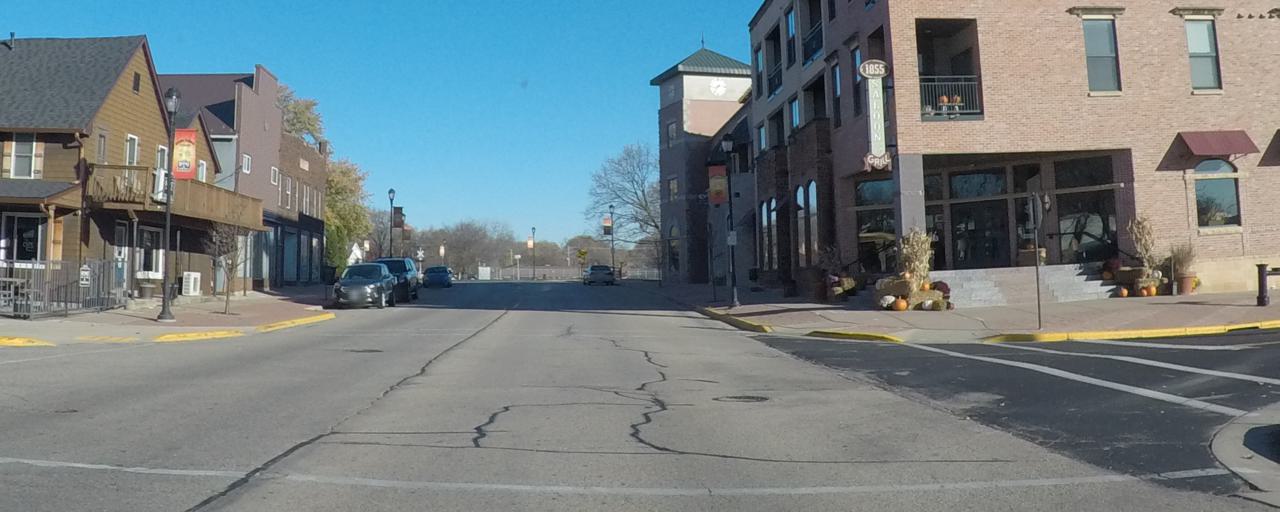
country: US
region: Wisconsin
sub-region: Dane County
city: Cottage Grove
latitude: 43.0753
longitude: -89.1997
